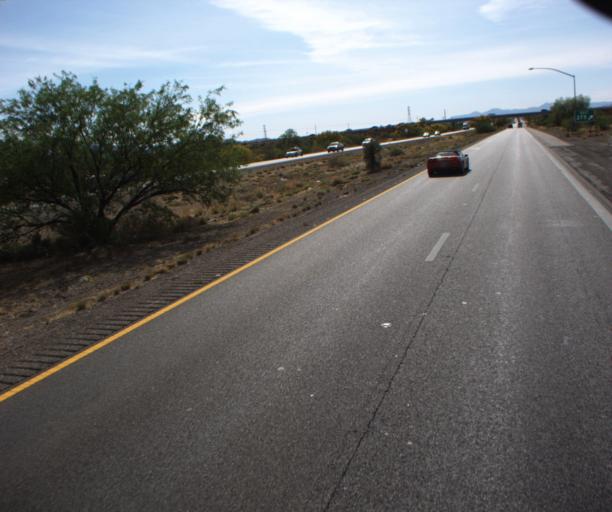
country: US
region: Arizona
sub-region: Pima County
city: Vail
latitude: 32.0634
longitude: -110.7769
